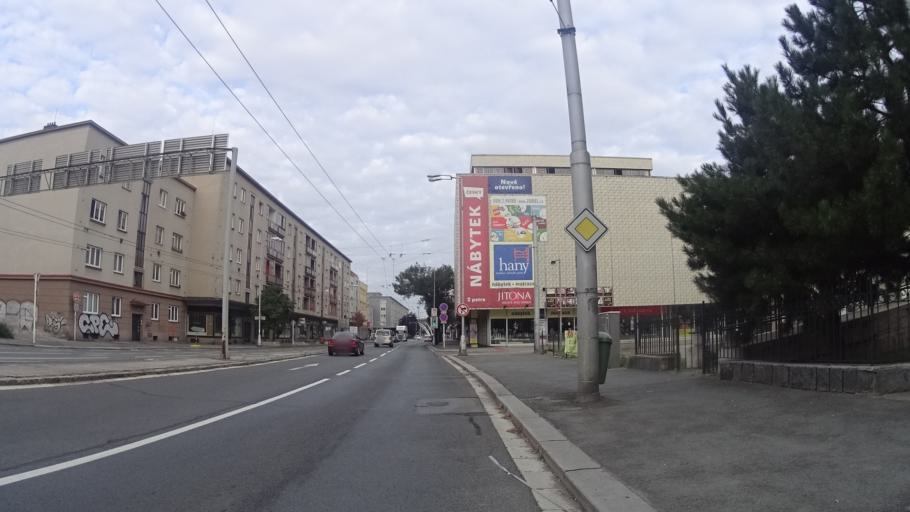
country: CZ
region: Kralovehradecky
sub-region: Okres Hradec Kralove
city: Hradec Kralove
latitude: 50.2112
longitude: 15.8197
